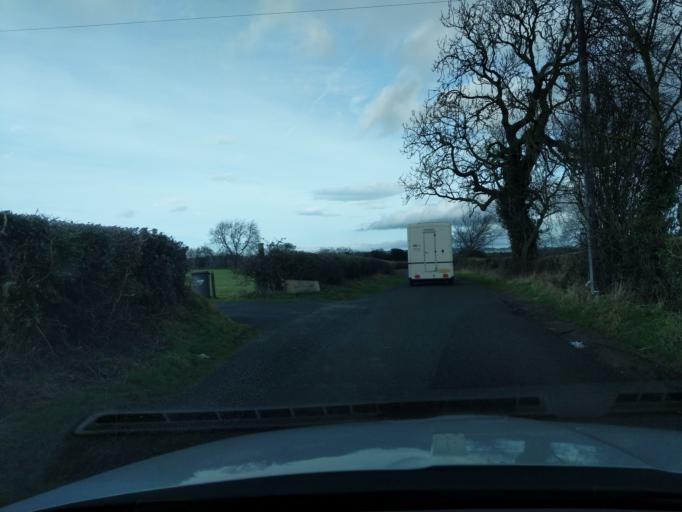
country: GB
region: England
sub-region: North Yorkshire
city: Catterick
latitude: 54.3620
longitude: -1.6649
